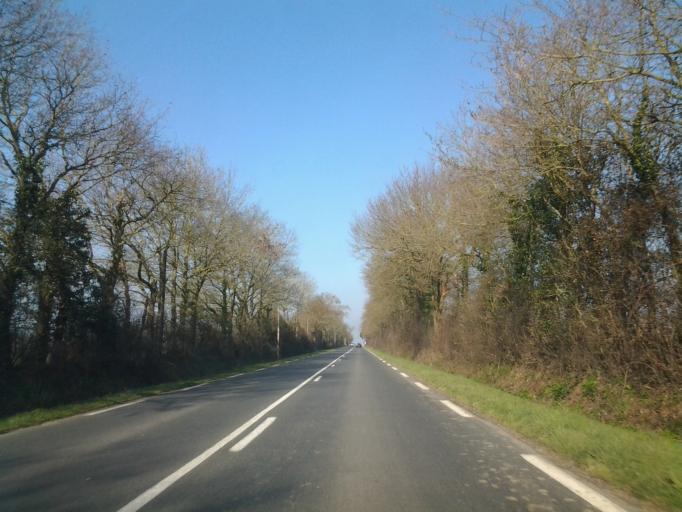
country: FR
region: Pays de la Loire
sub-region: Departement de la Vendee
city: Mache
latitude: 46.7836
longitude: -1.6929
